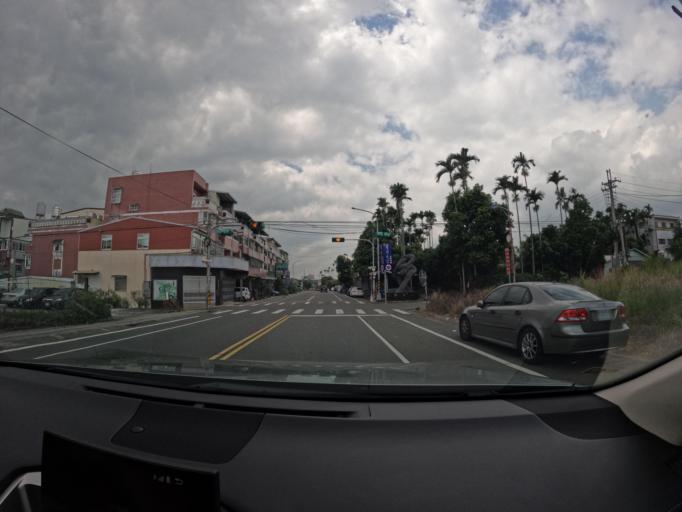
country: TW
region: Taiwan
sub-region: Nantou
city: Nantou
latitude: 23.9091
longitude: 120.6370
